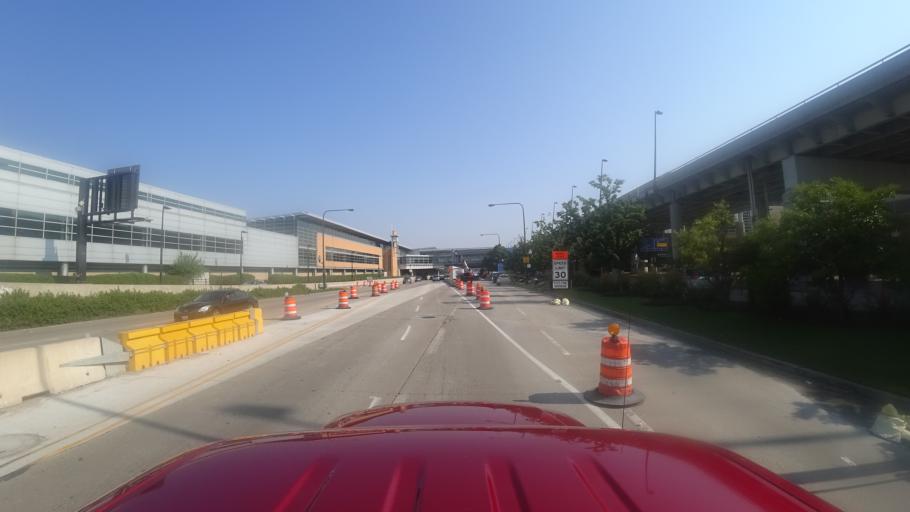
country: US
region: Illinois
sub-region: Cook County
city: Hometown
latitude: 41.7867
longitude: -87.7413
